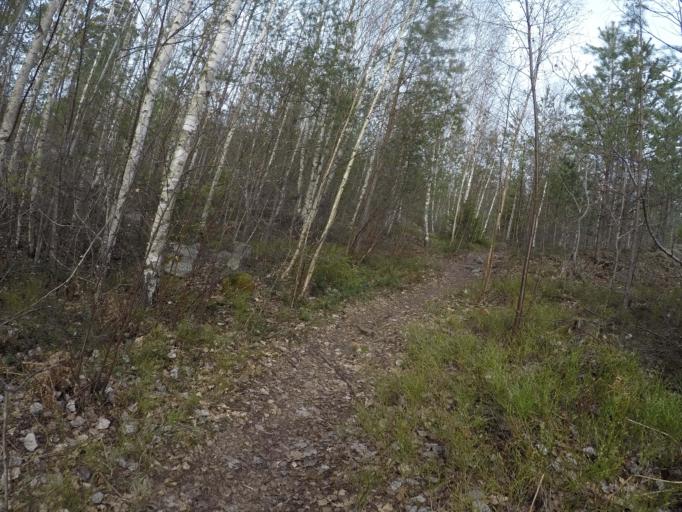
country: SE
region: Soedermanland
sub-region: Eskilstuna Kommun
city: Torshalla
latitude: 59.4389
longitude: 16.5131
